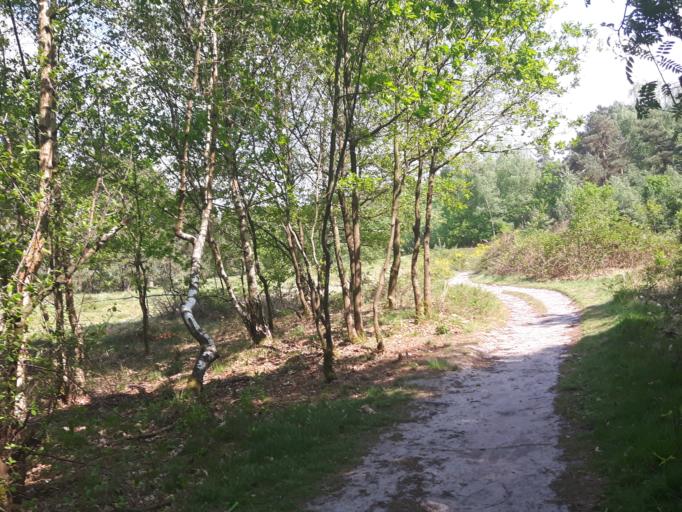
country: NL
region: Overijssel
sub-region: Gemeente Enschede
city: Enschede
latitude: 52.1379
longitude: 6.8725
